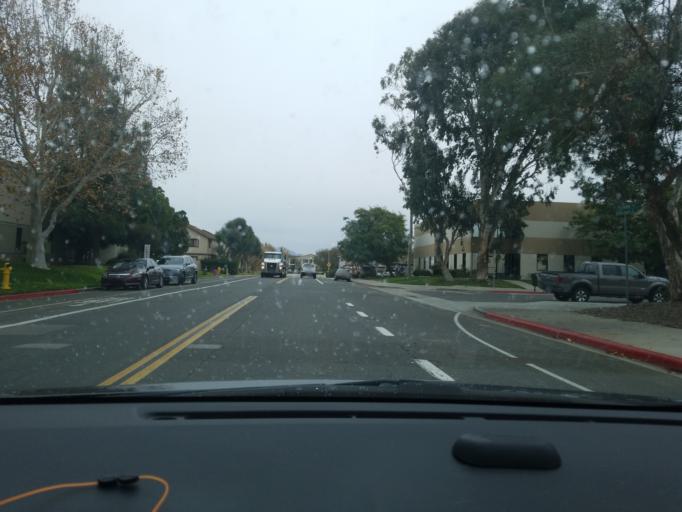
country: US
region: California
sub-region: Riverside County
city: Temecula
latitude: 33.4955
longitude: -117.1542
